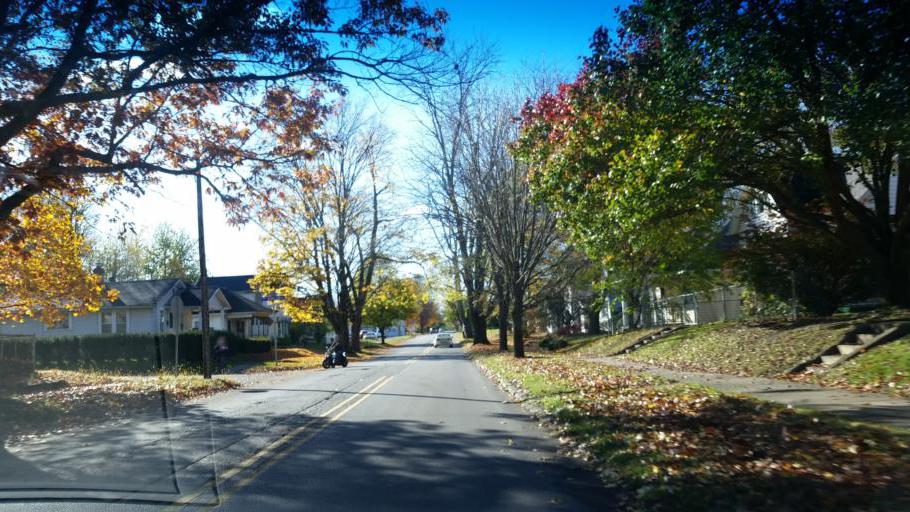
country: US
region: Indiana
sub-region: Howard County
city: Kokomo
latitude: 40.4711
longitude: -86.1365
